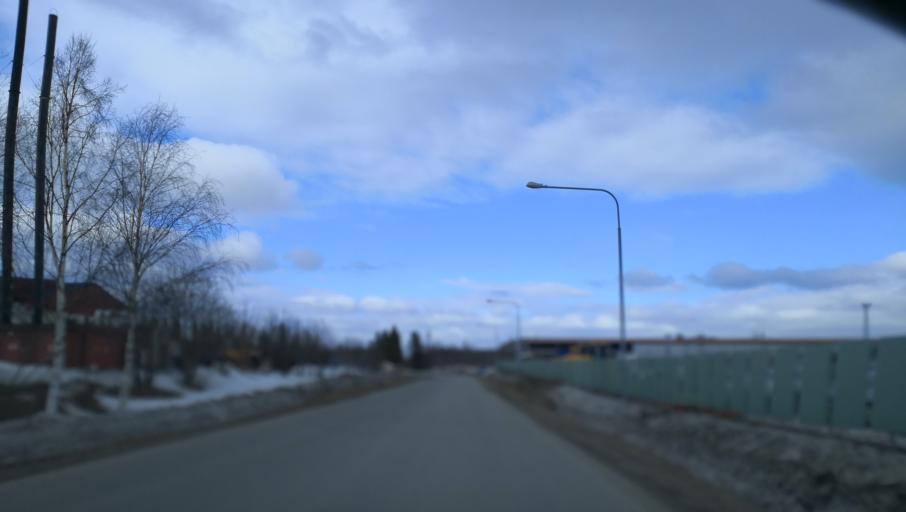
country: SE
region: Vaesterbotten
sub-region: Vannas Kommun
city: Vaennaes
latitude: 63.9152
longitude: 19.7437
